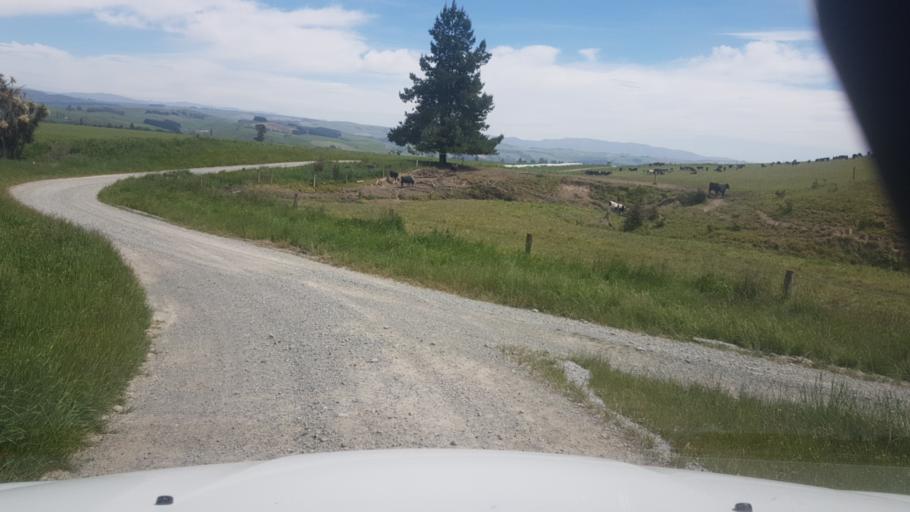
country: NZ
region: Canterbury
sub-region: Timaru District
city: Pleasant Point
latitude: -44.1703
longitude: 171.0212
